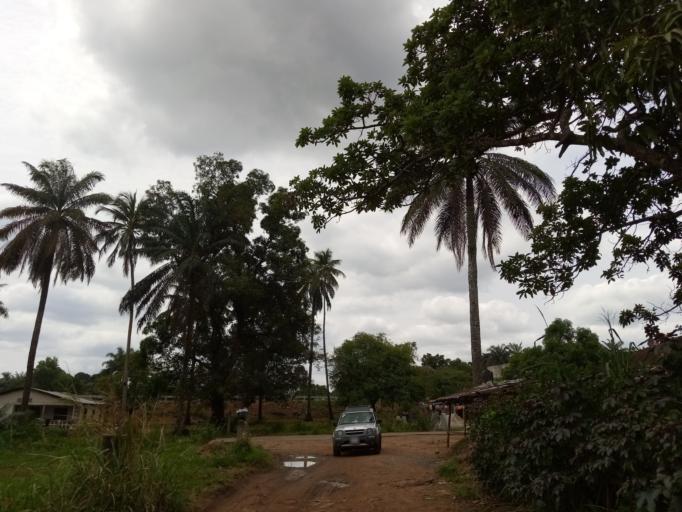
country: SL
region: Western Area
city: Waterloo
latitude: 8.3340
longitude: -13.0116
